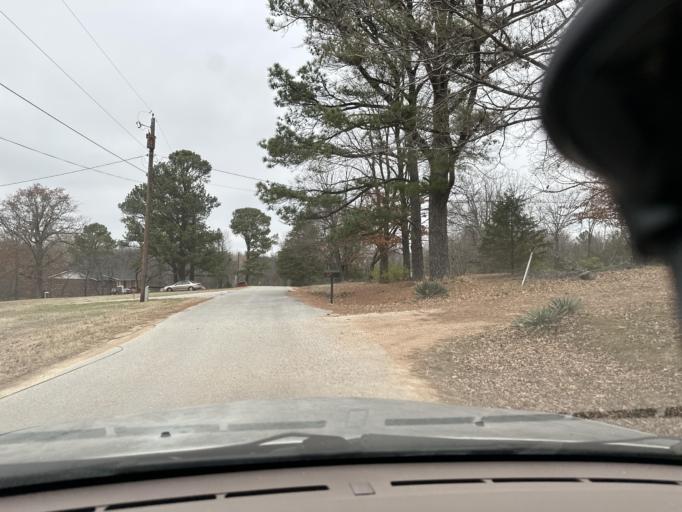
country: US
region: Arkansas
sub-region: Washington County
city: Fayetteville
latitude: 36.0891
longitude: -94.1197
